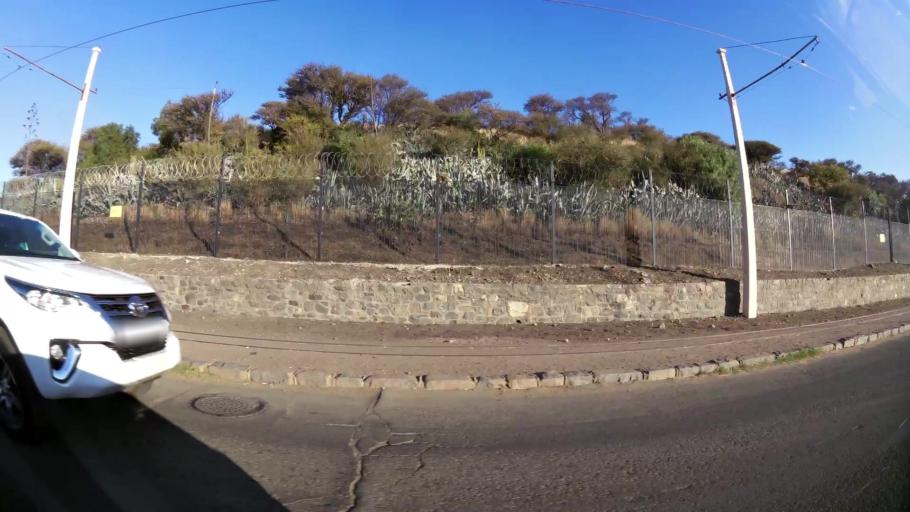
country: ZA
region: Northern Cape
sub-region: Frances Baard District Municipality
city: Kimberley
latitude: -28.7364
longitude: 24.7560
